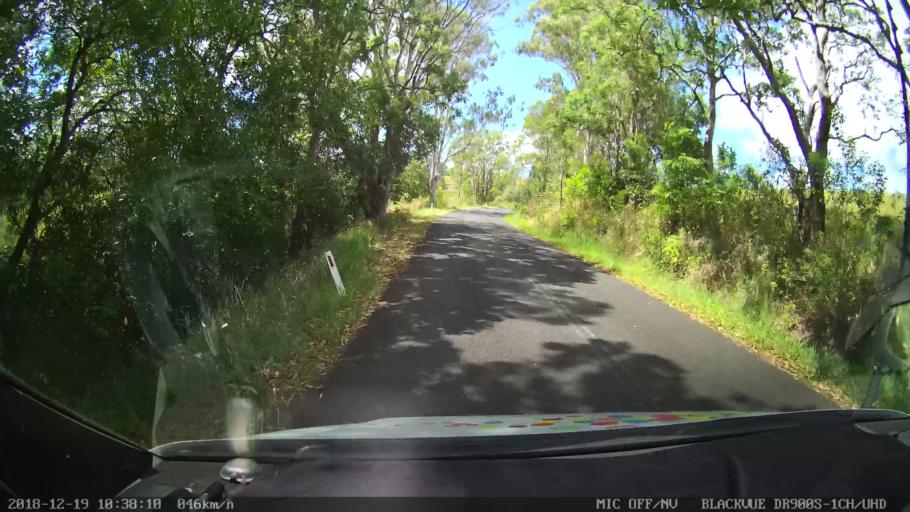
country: AU
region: New South Wales
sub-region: Lismore Municipality
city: Nimbin
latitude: -28.5733
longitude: 153.1546
